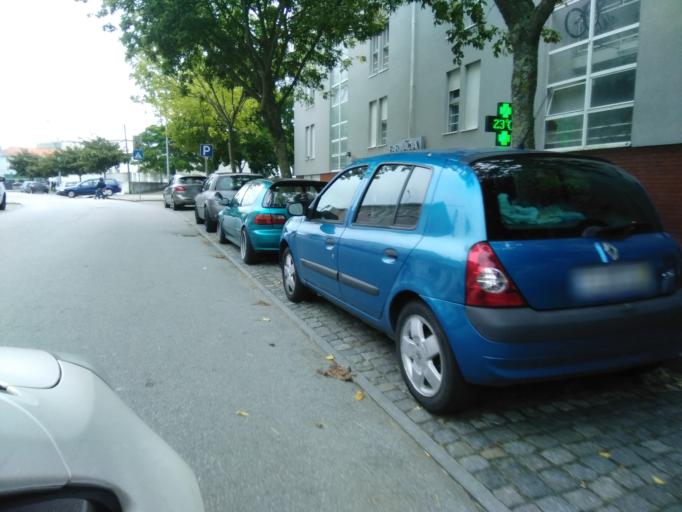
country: PT
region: Porto
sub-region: Matosinhos
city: Santa Cruz do Bispo
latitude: 41.2244
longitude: -8.6997
